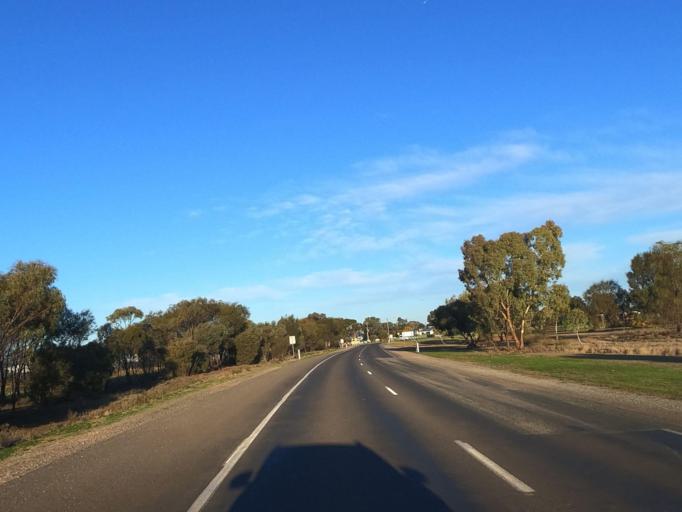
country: AU
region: Victoria
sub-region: Swan Hill
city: Swan Hill
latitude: -35.3380
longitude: 143.5386
